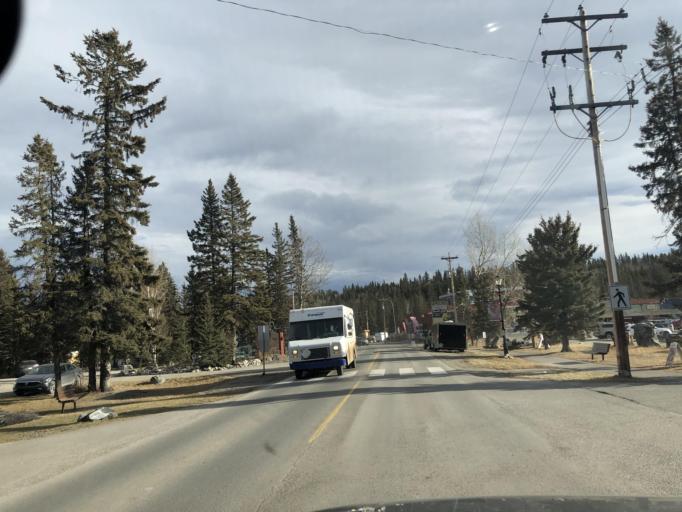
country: CA
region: Alberta
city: Cochrane
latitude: 50.9526
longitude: -114.5627
